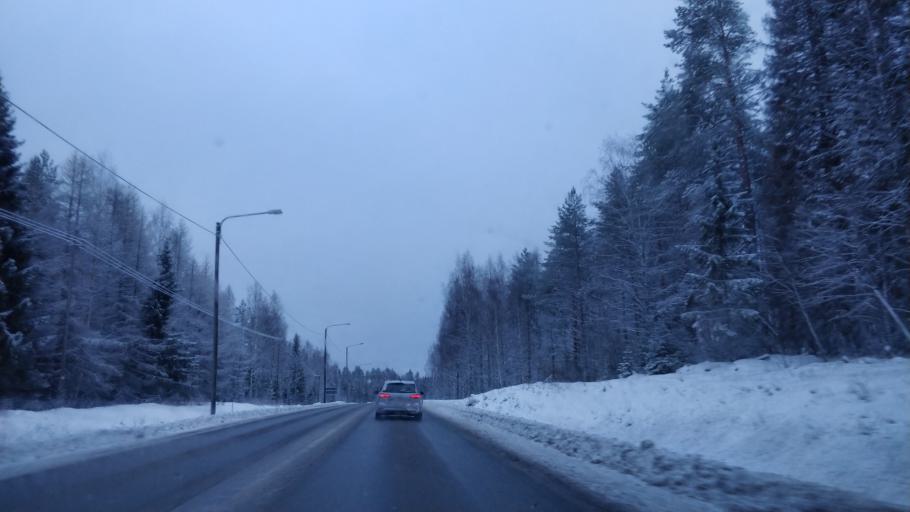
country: FI
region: Central Finland
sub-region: Saarijaervi-Viitasaari
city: Viitasaari
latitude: 63.1836
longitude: 25.7216
